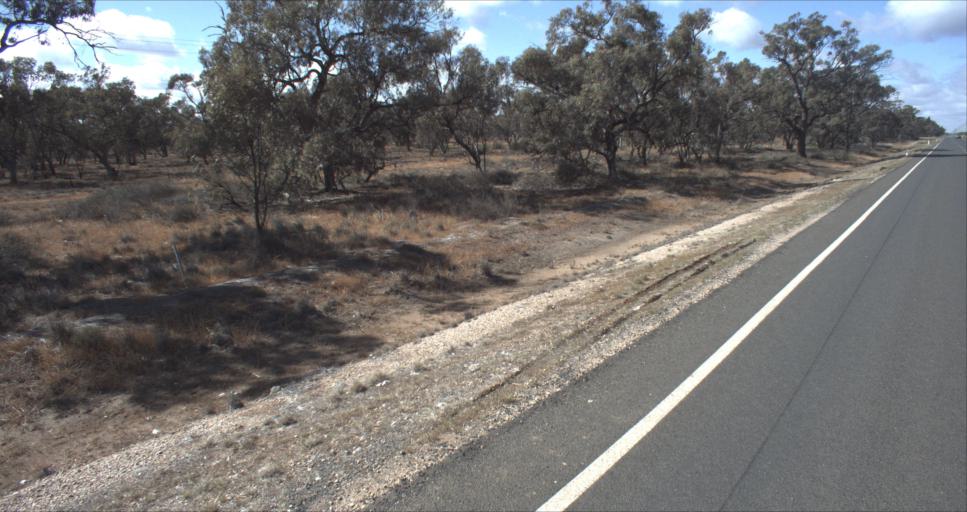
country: AU
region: New South Wales
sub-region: Murrumbidgee Shire
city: Darlington Point
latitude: -34.5218
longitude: 146.1756
